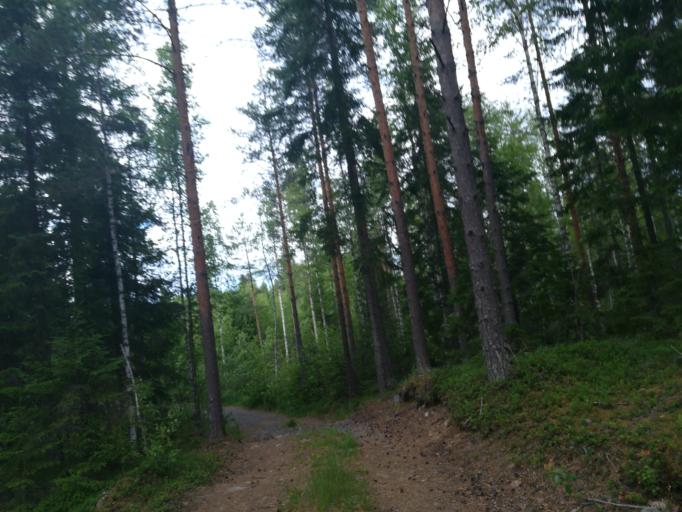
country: FI
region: Southern Savonia
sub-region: Mikkeli
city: Mikkeli
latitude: 61.6715
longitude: 27.1115
